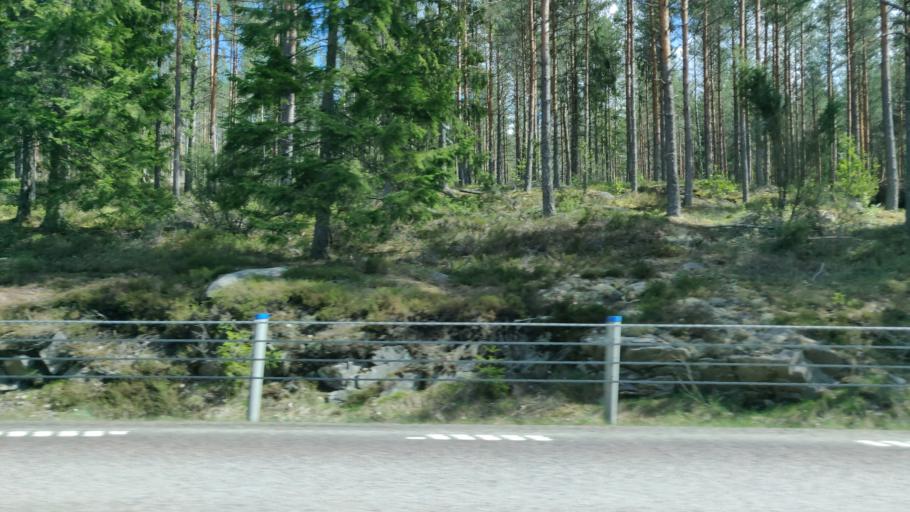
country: SE
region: Vaermland
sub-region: Karlstads Kommun
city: Molkom
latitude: 59.5757
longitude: 13.6677
